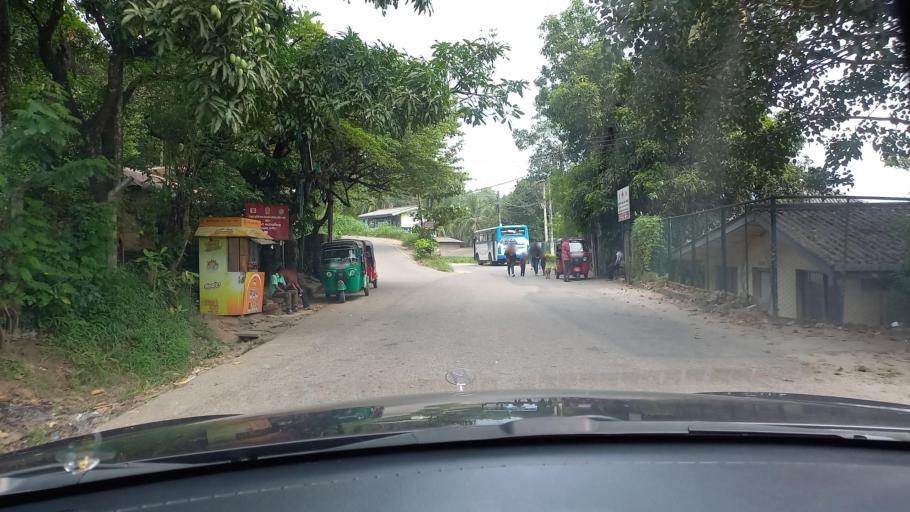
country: LK
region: Central
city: Kandy
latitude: 7.2308
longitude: 80.6051
